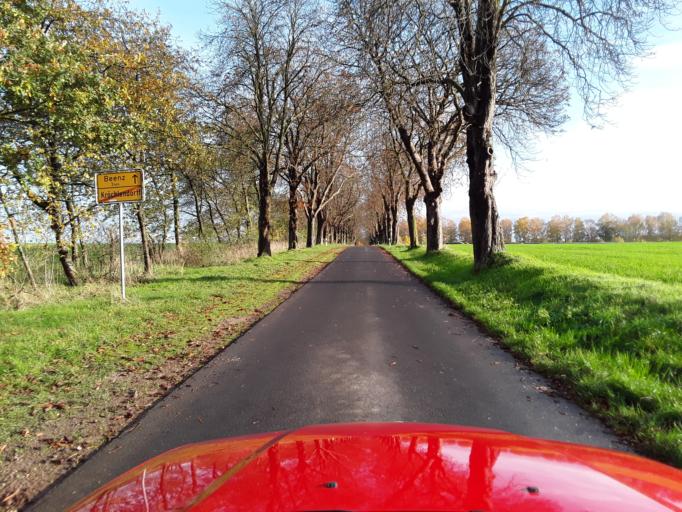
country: DE
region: Brandenburg
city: Mittenwalde
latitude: 53.2704
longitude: 13.6992
